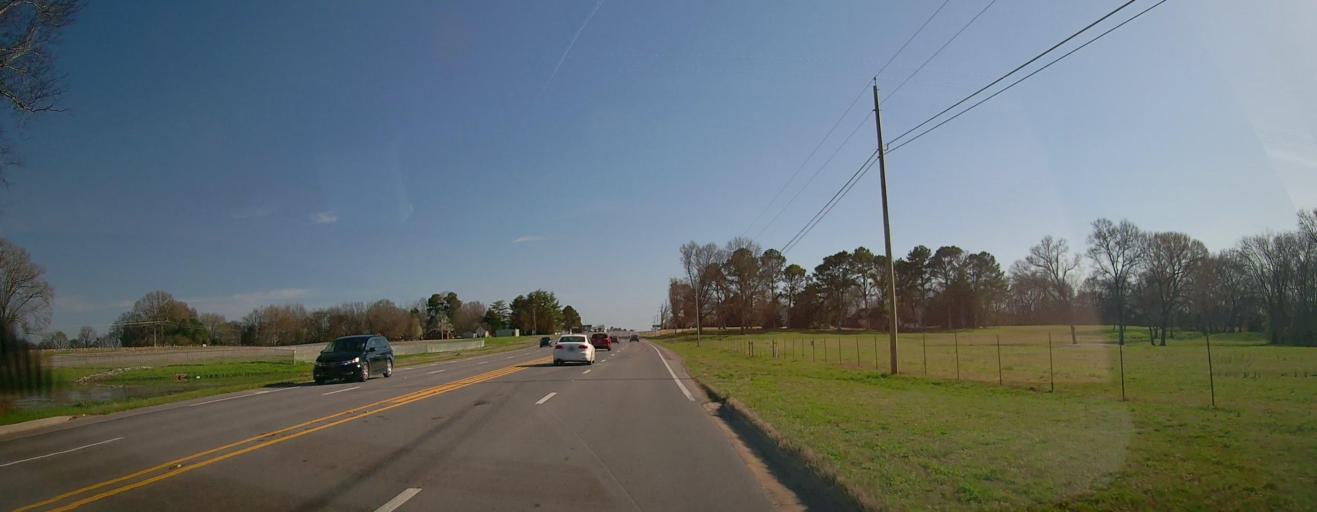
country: US
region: Alabama
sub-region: Colbert County
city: Muscle Shoals
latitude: 34.7127
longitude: -87.6350
